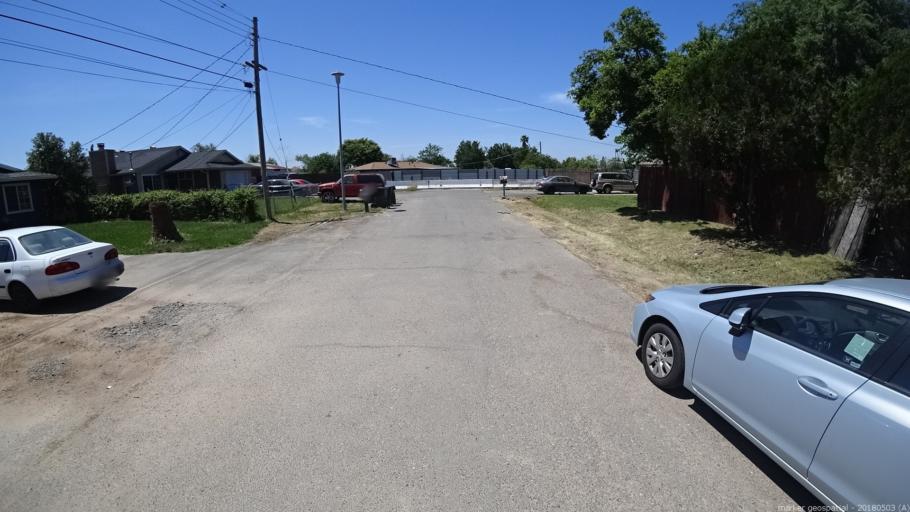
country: US
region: California
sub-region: Sacramento County
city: Rio Linda
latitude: 38.6449
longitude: -121.4333
